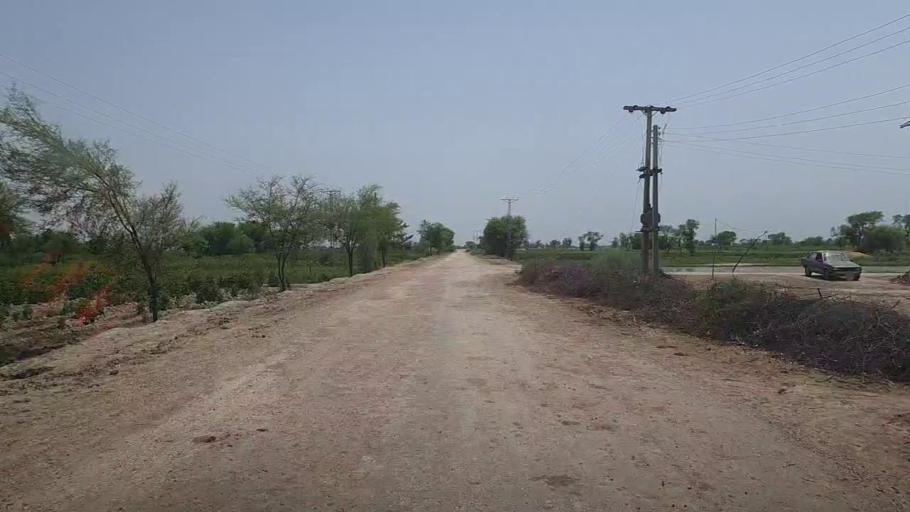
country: PK
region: Sindh
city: Pad Idan
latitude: 26.8319
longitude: 68.3086
